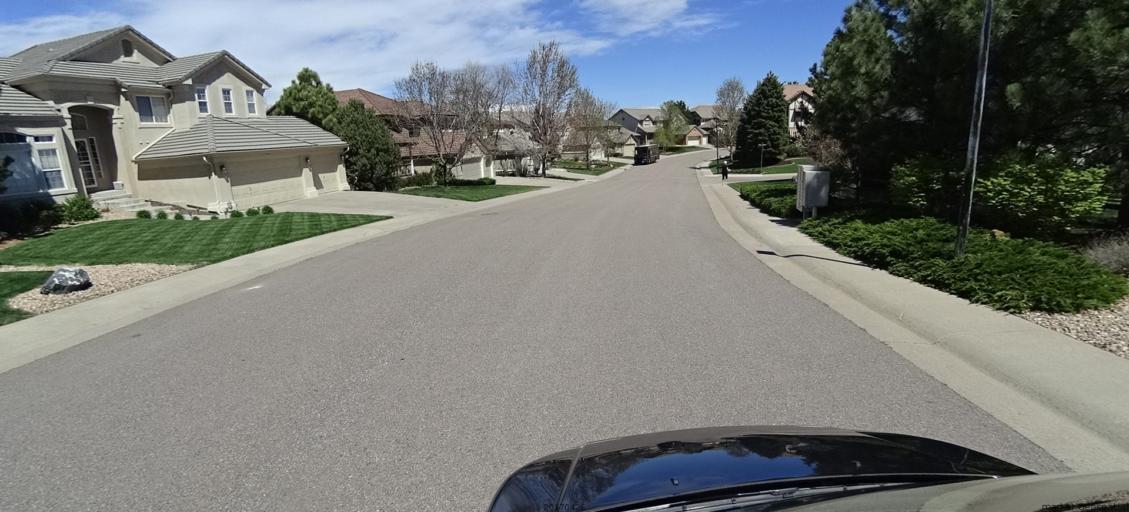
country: US
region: Colorado
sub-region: Adams County
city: Lone Tree
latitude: 39.5385
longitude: -104.8890
